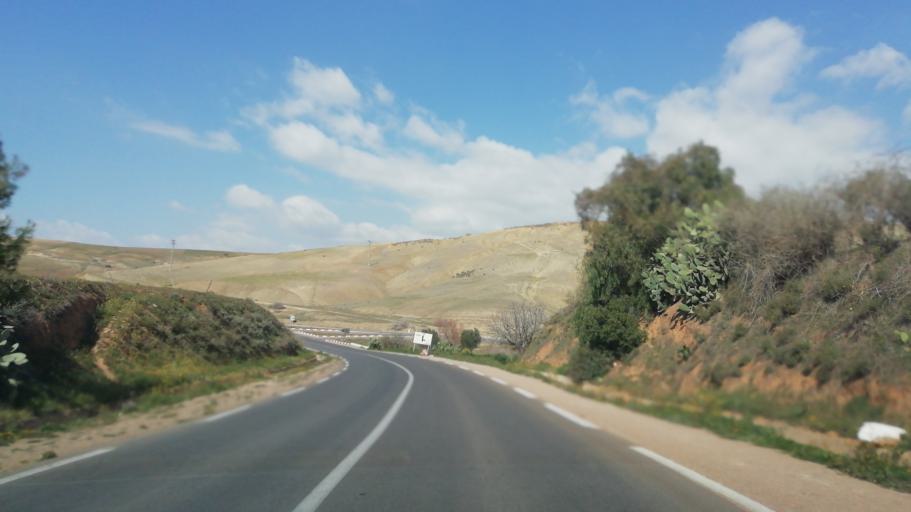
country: DZ
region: Mascara
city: Mascara
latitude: 35.5384
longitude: 0.1137
